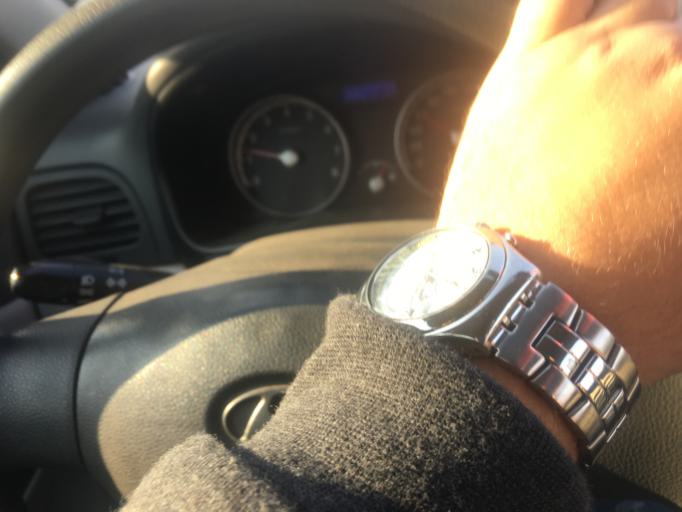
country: EG
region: Muhafazat al Qahirah
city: Cairo
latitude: 30.0369
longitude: 31.2705
